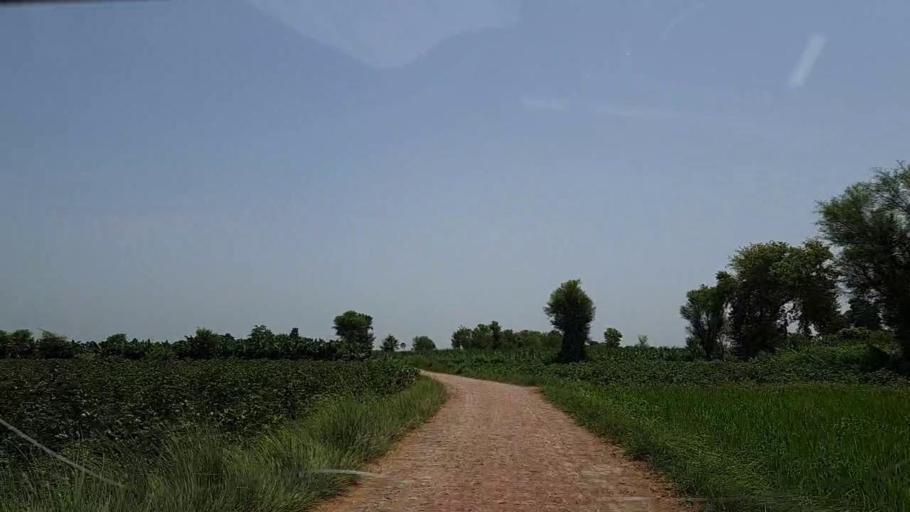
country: PK
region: Sindh
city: Tharu Shah
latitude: 26.9327
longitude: 68.0391
